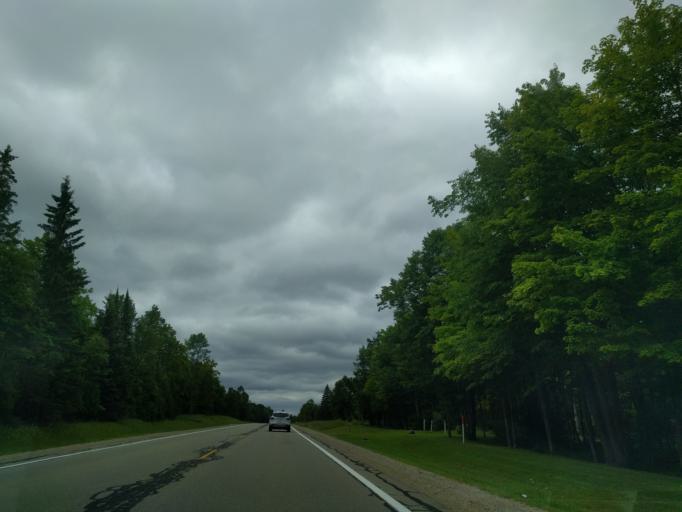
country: US
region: Michigan
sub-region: Menominee County
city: Menominee
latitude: 45.3628
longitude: -87.3978
